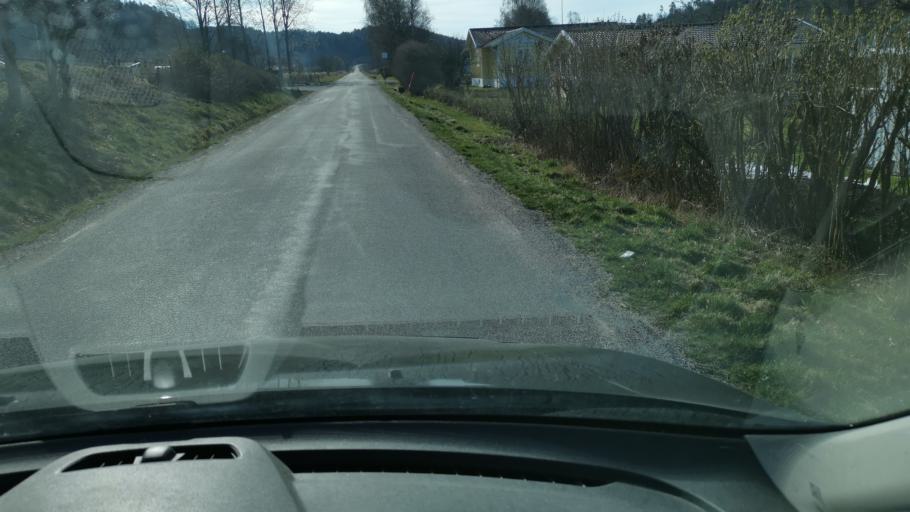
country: SE
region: Vaestra Goetaland
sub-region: Lysekils Kommun
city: Brastad
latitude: 58.3450
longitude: 11.5906
